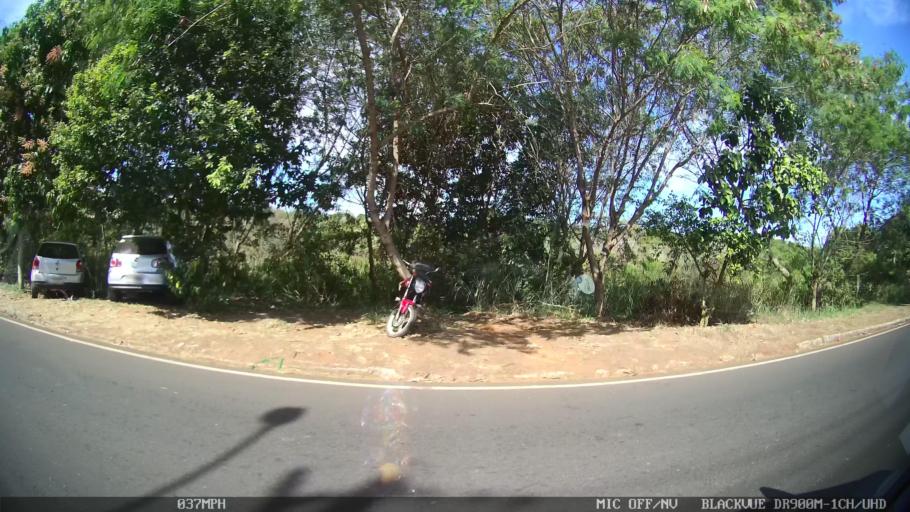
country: BR
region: Sao Paulo
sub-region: Sao Jose Do Rio Preto
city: Sao Jose do Rio Preto
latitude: -20.8459
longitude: -49.3600
